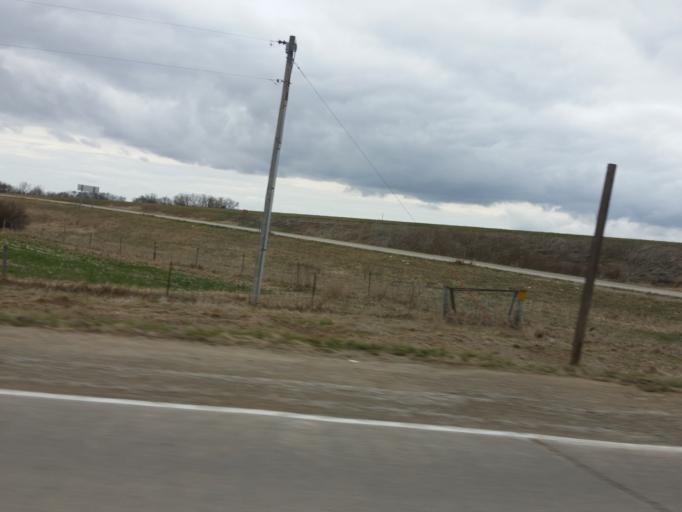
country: US
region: Iowa
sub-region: Benton County
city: Urbana
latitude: 42.3120
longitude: -91.9797
